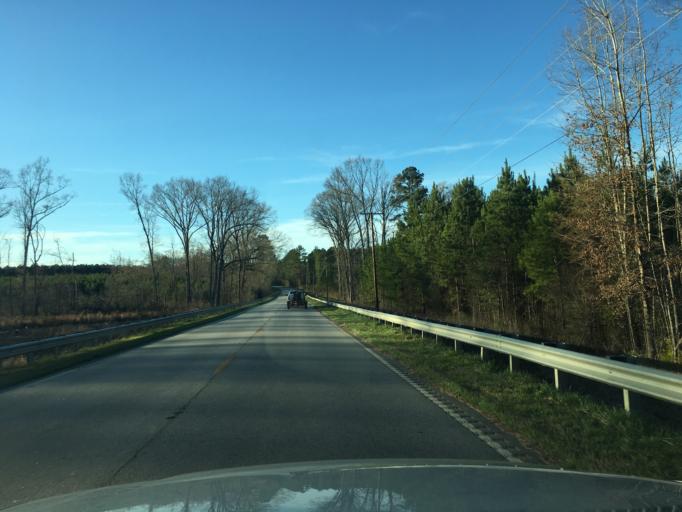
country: US
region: South Carolina
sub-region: Saluda County
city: Saluda
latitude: 34.0360
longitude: -81.8068
